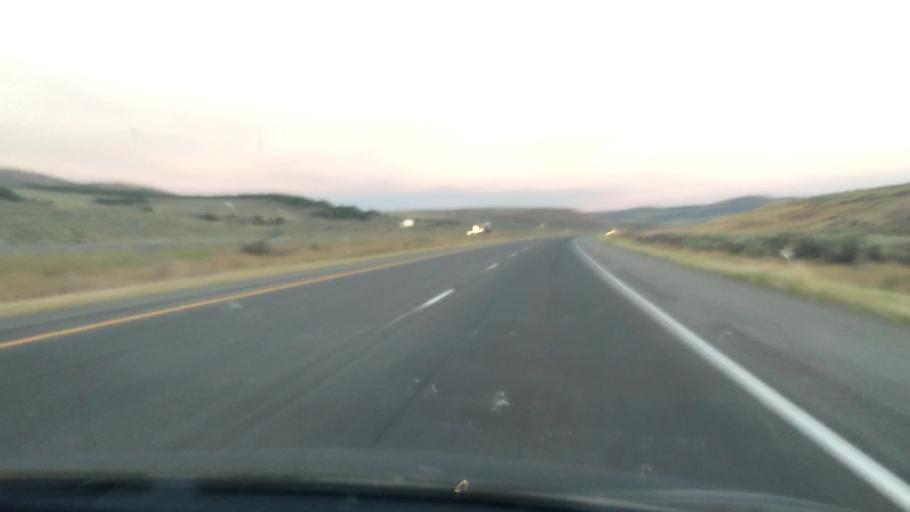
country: US
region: Idaho
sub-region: Power County
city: American Falls
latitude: 42.2521
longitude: -113.1050
